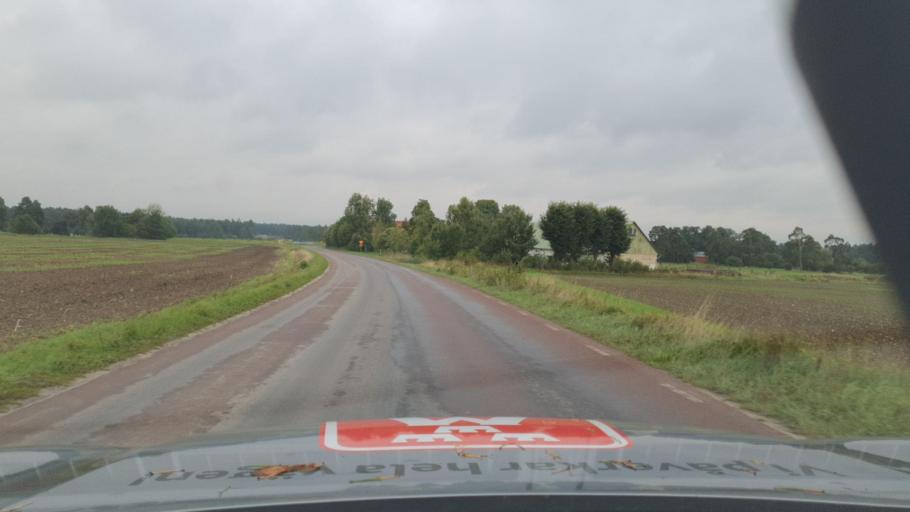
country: SE
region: Gotland
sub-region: Gotland
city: Visby
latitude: 57.6445
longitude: 18.5527
